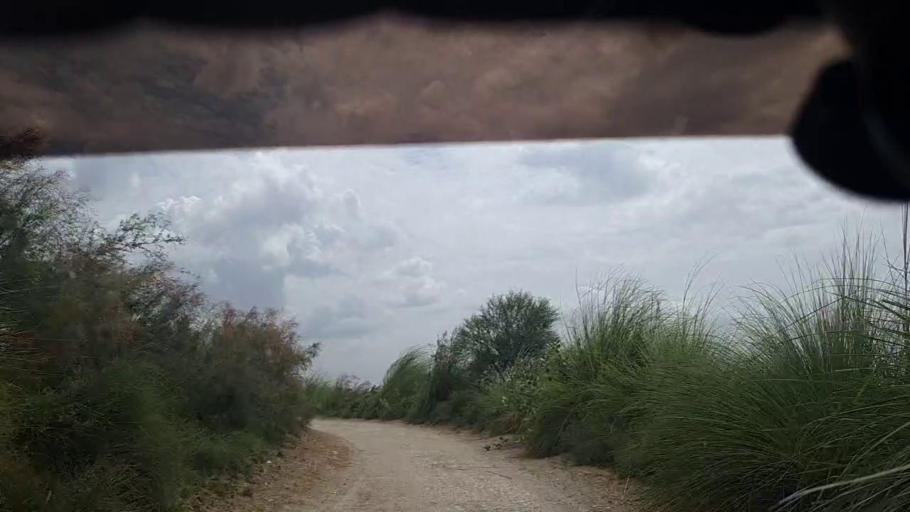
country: PK
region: Sindh
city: Rustam jo Goth
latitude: 28.0504
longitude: 68.9393
